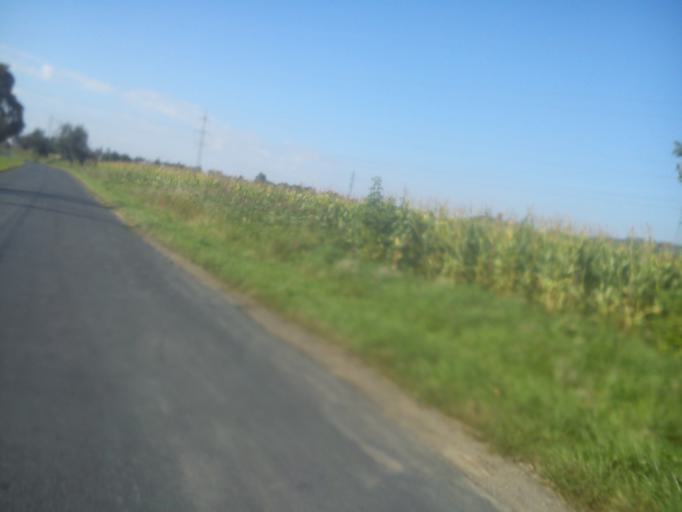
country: CZ
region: South Moravian
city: Telnice
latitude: 49.0986
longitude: 16.7415
